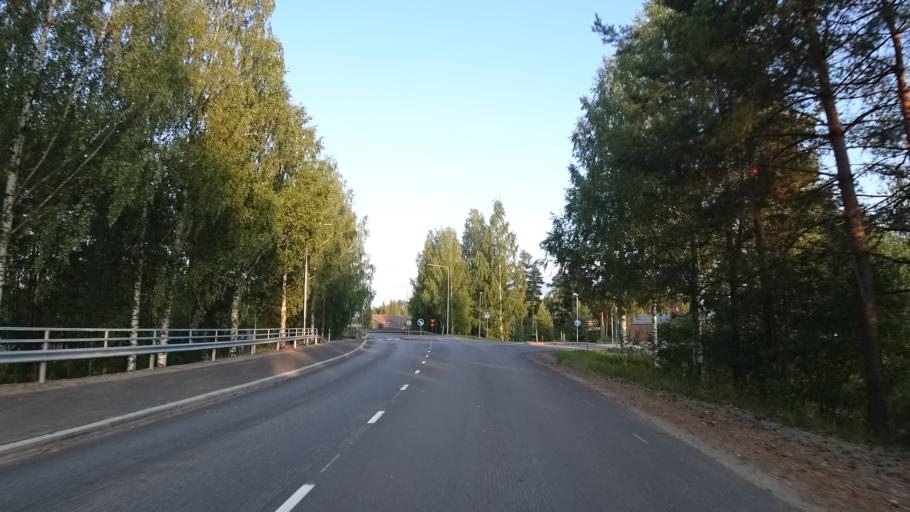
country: FI
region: Southern Savonia
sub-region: Savonlinna
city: Punkaharju
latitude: 61.7565
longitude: 29.3875
